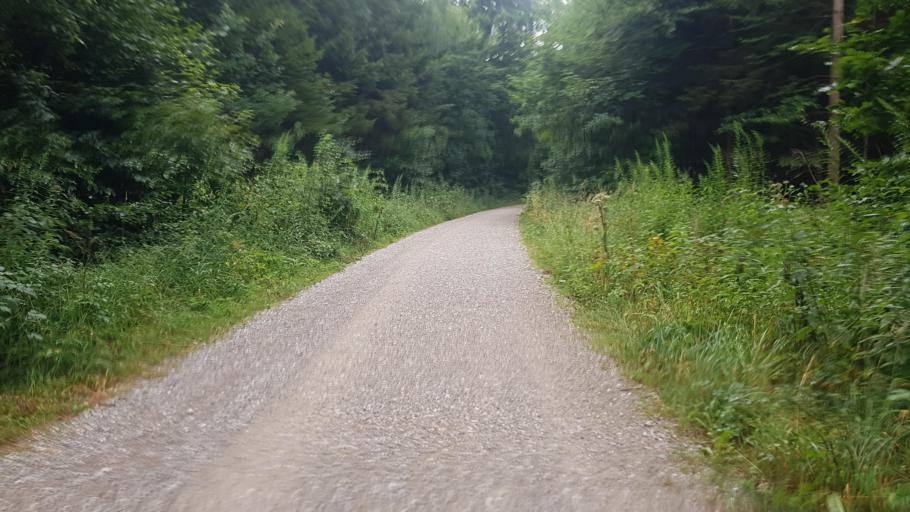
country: DE
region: Bavaria
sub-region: Upper Bavaria
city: Starnberg
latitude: 48.0255
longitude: 11.3417
